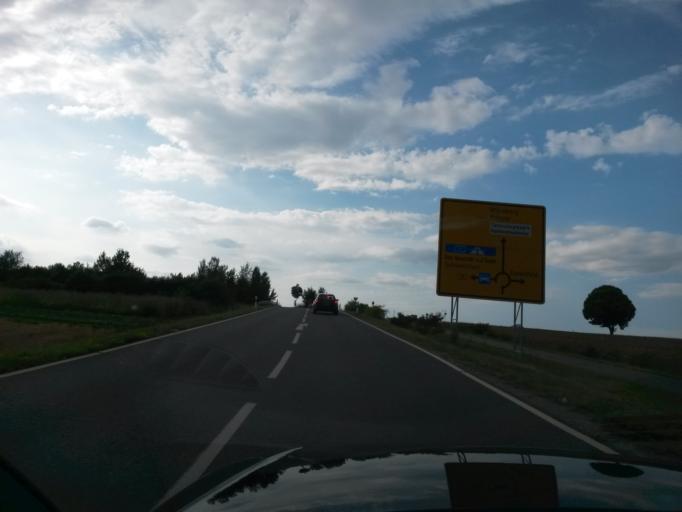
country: DE
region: Bavaria
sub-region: Regierungsbezirk Unterfranken
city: Estenfeld
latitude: 49.8236
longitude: 9.9934
